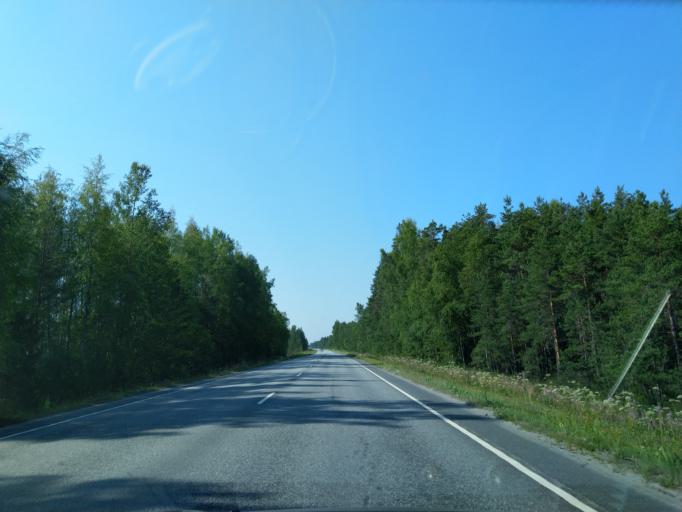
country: FI
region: Satakunta
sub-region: Pori
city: Pomarkku
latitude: 61.6840
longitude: 21.9918
